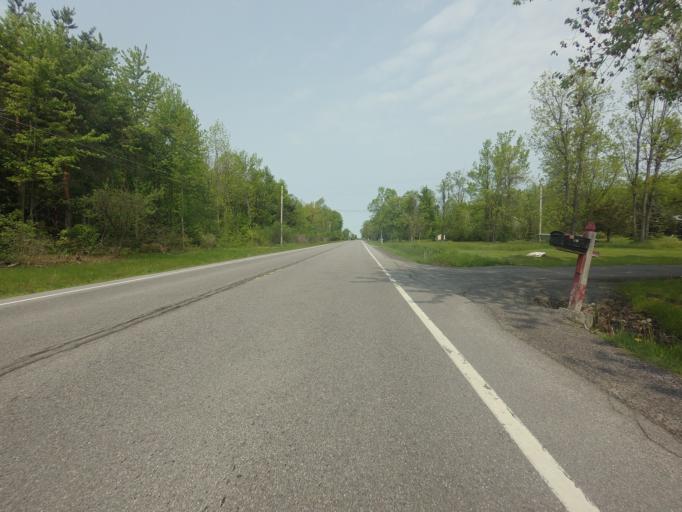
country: US
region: New York
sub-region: Jefferson County
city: Dexter
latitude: 44.0183
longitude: -76.0283
